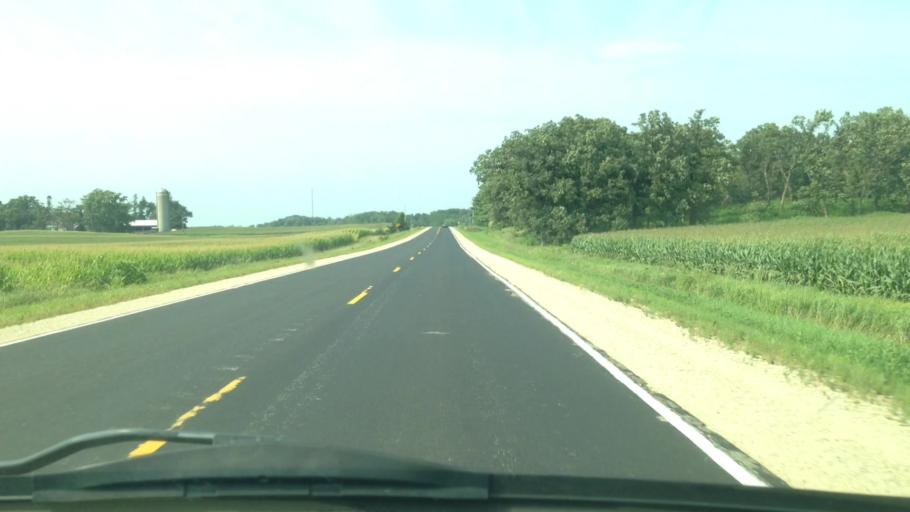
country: US
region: Minnesota
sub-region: Winona County
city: Lewiston
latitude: 43.9153
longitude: -91.9593
